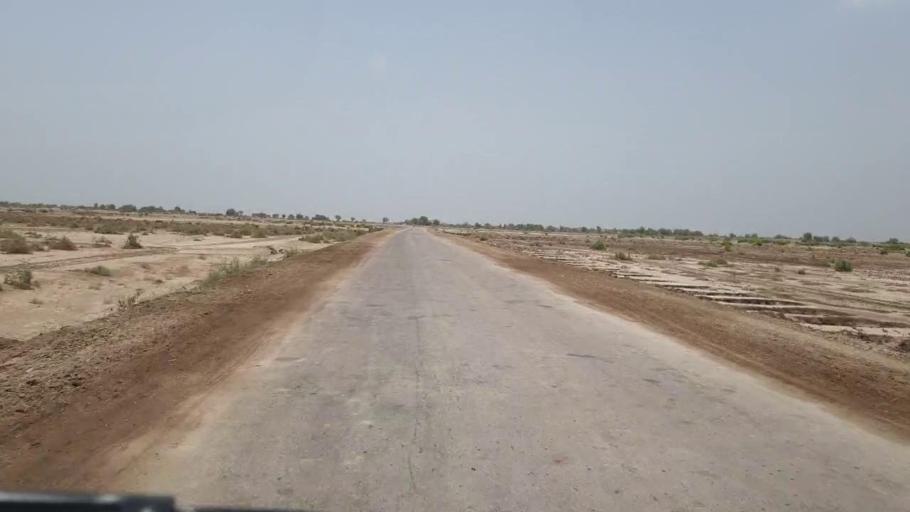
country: PK
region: Sindh
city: Daulatpur
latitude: 26.4519
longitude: 68.1174
